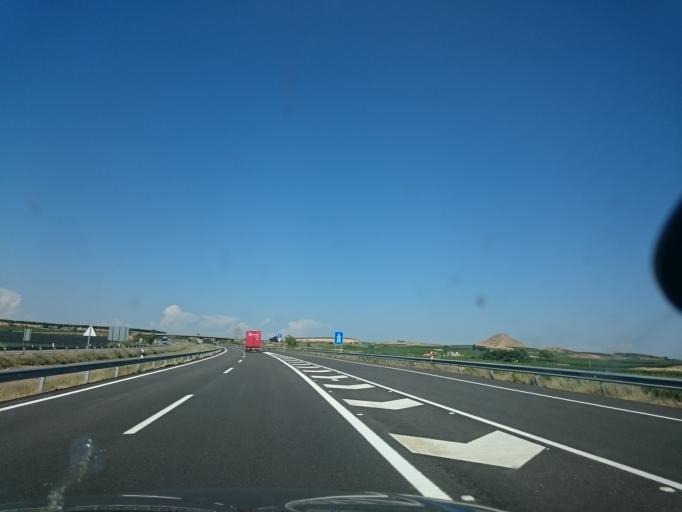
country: ES
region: Catalonia
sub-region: Provincia de Lleida
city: Seros
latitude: 41.4982
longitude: 0.3986
